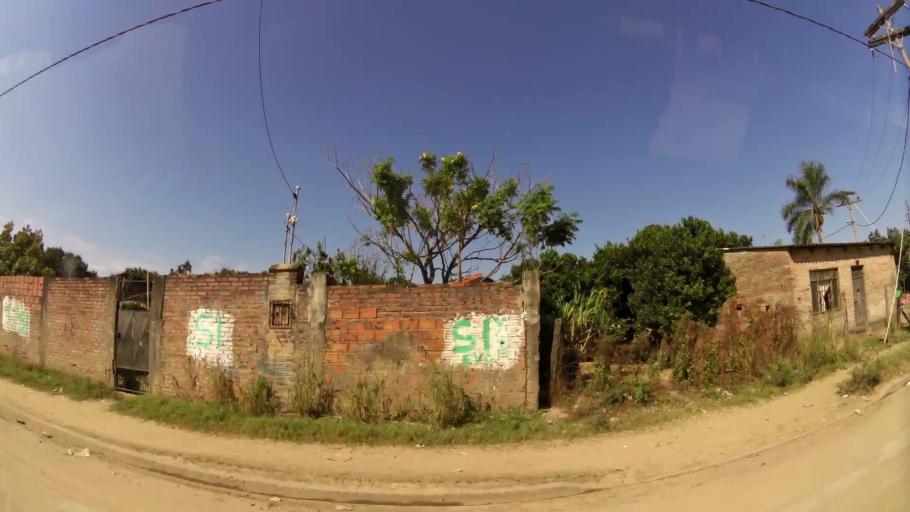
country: BO
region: Santa Cruz
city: Cotoca
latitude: -17.7381
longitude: -63.0741
